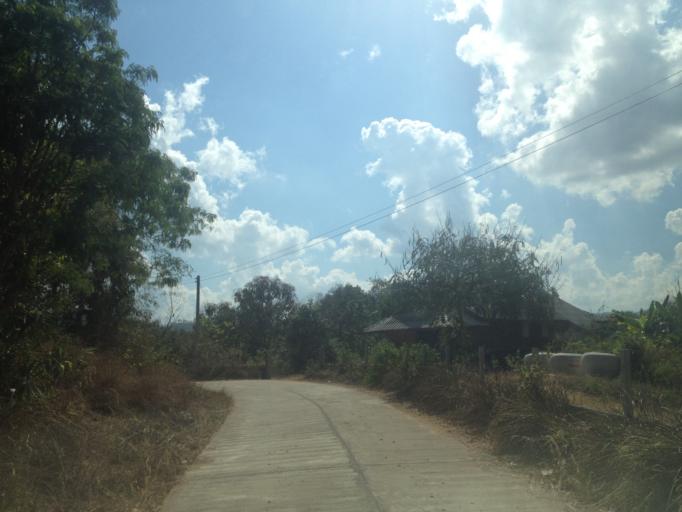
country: TH
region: Mae Hong Son
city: Ban Huai I Huak
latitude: 18.0904
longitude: 98.1935
